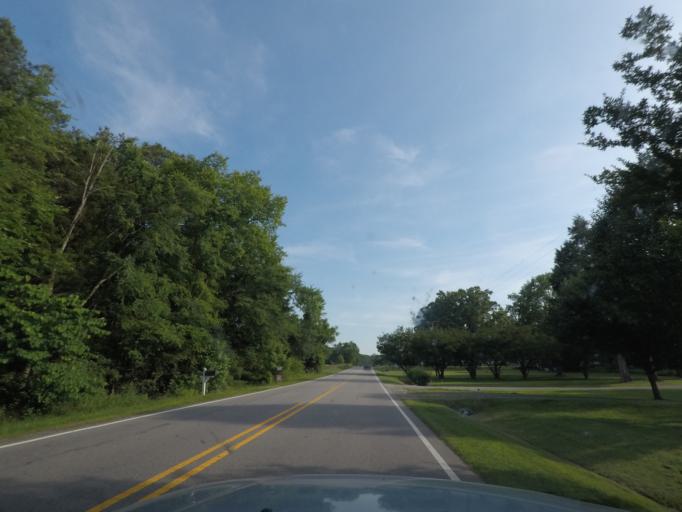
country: US
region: Virginia
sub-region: Mecklenburg County
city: Clarksville
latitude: 36.4962
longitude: -78.5430
